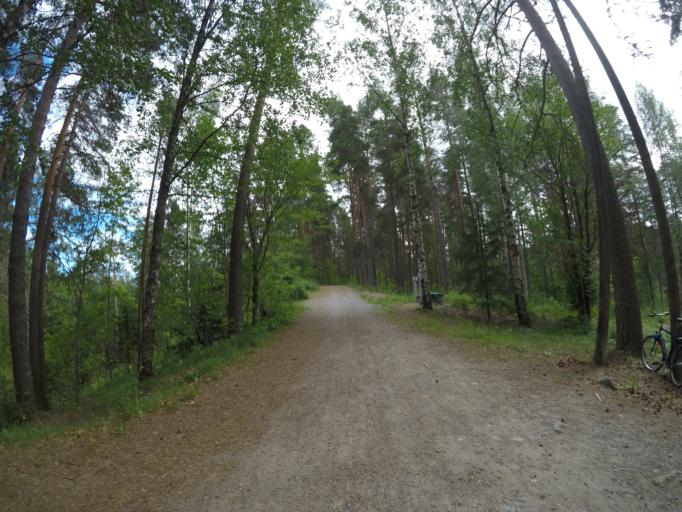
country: FI
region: Haeme
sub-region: Haemeenlinna
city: Haemeenlinna
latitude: 60.9931
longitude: 24.4229
